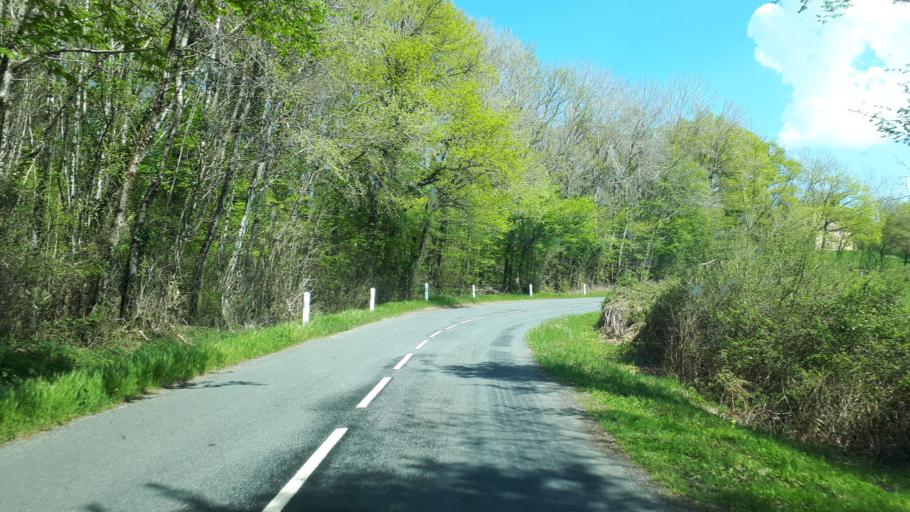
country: FR
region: Centre
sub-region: Departement du Cher
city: Rians
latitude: 47.3000
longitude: 2.6706
